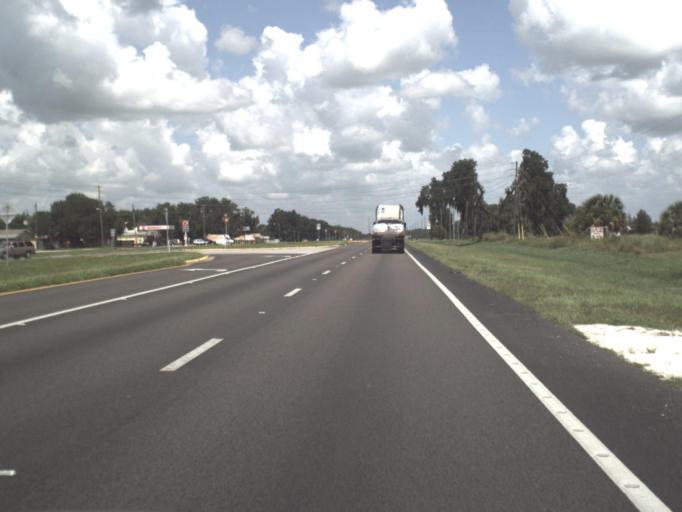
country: US
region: Florida
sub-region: Hardee County
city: Wauchula
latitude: 27.5729
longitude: -81.8167
